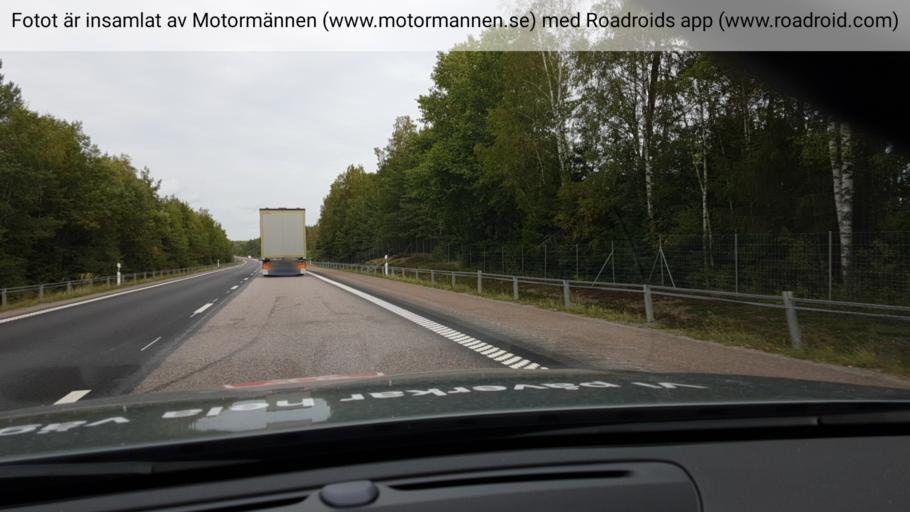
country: SE
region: Stockholm
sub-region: Sigtuna Kommun
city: Marsta
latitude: 59.6557
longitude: 17.8879
